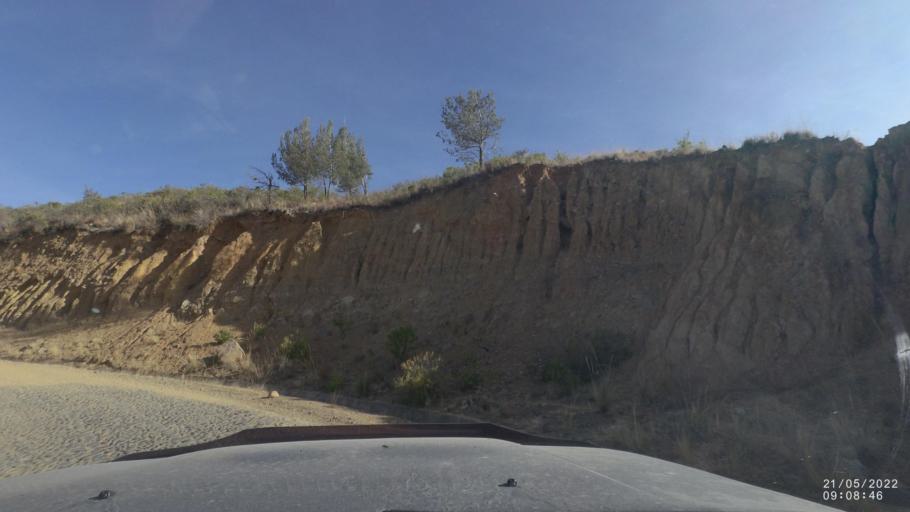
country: BO
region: Cochabamba
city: Cochabamba
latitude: -17.3754
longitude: -66.0221
